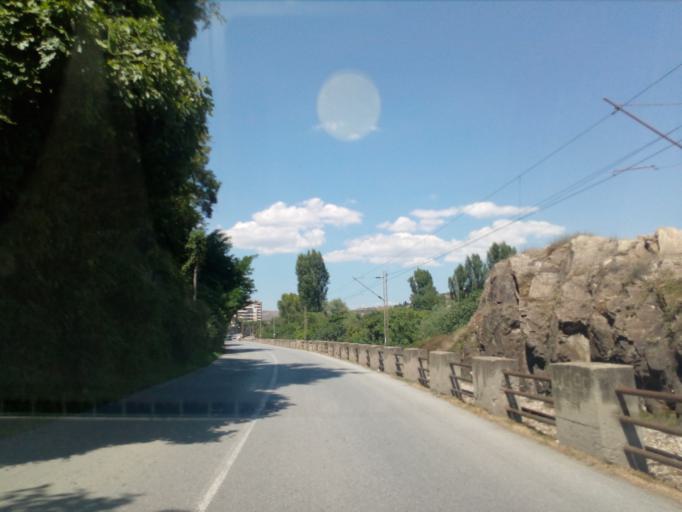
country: MK
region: Veles
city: Veles
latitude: 41.7097
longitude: 21.7846
